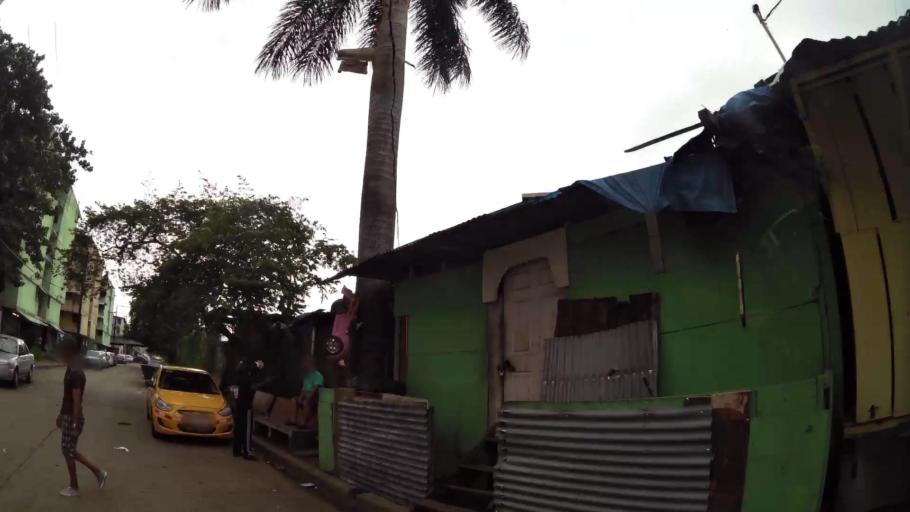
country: PA
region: Panama
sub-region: Distrito de Panama
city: Ancon
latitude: 8.9671
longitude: -79.5455
